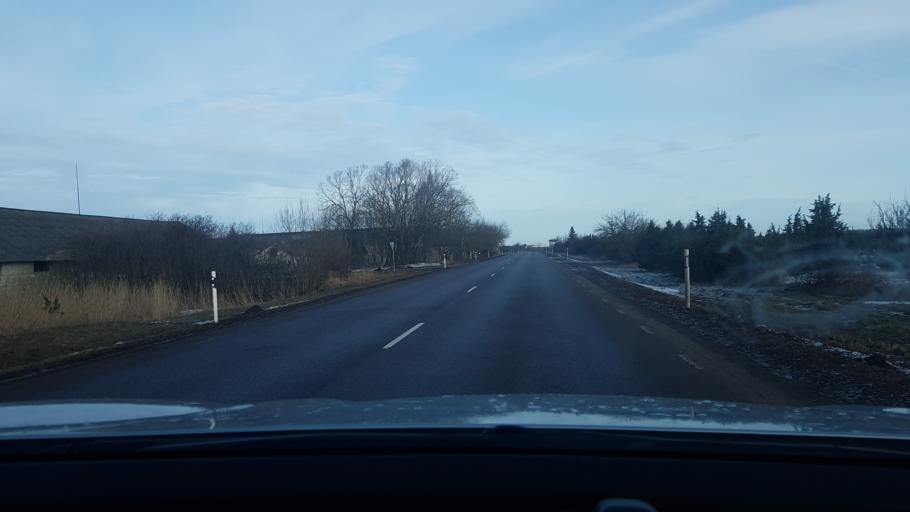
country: EE
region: Saare
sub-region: Kuressaare linn
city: Kuressaare
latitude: 58.2247
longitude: 22.5062
